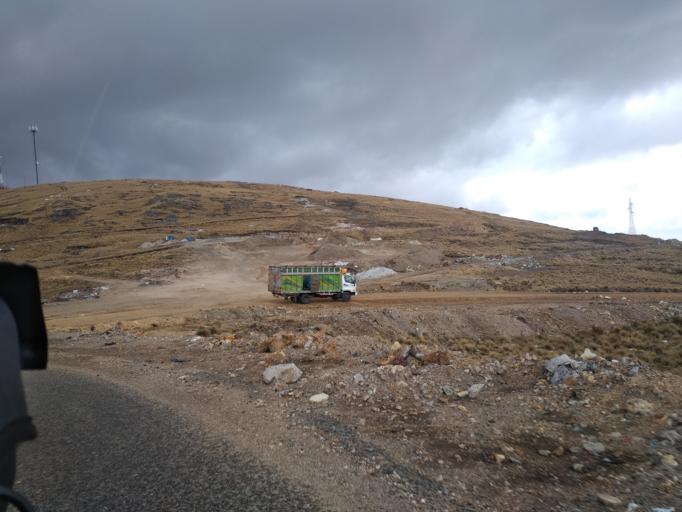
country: PE
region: La Libertad
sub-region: Provincia de Santiago de Chuco
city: Quiruvilca
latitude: -7.9960
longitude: -78.3102
